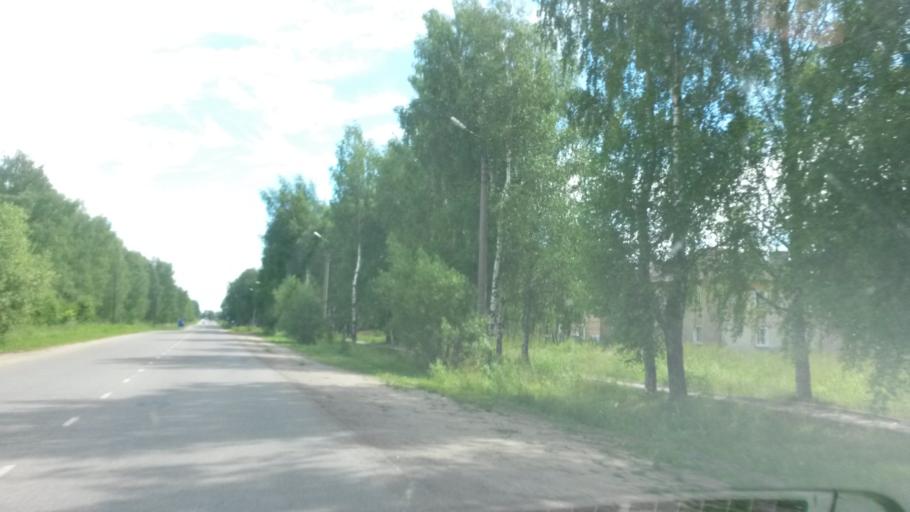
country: RU
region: Ivanovo
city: Zavolzhsk
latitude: 57.4736
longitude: 42.1560
